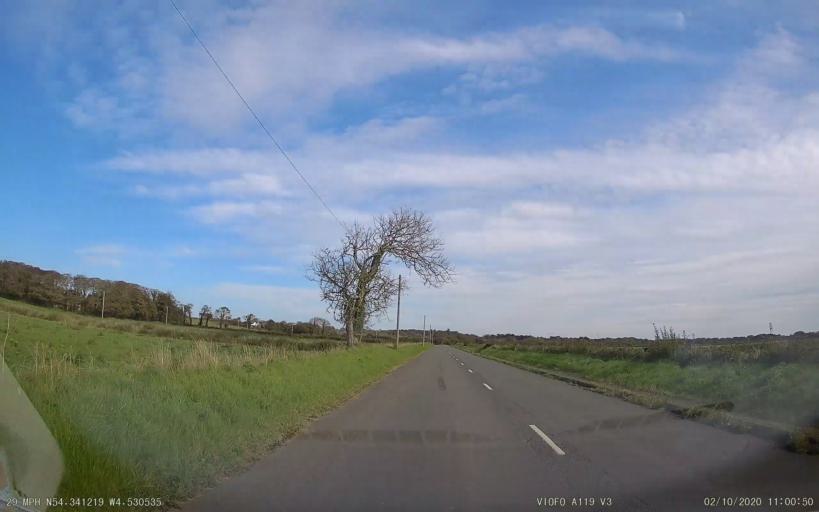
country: IM
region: Ramsey
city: Ramsey
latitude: 54.3412
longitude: -4.5305
